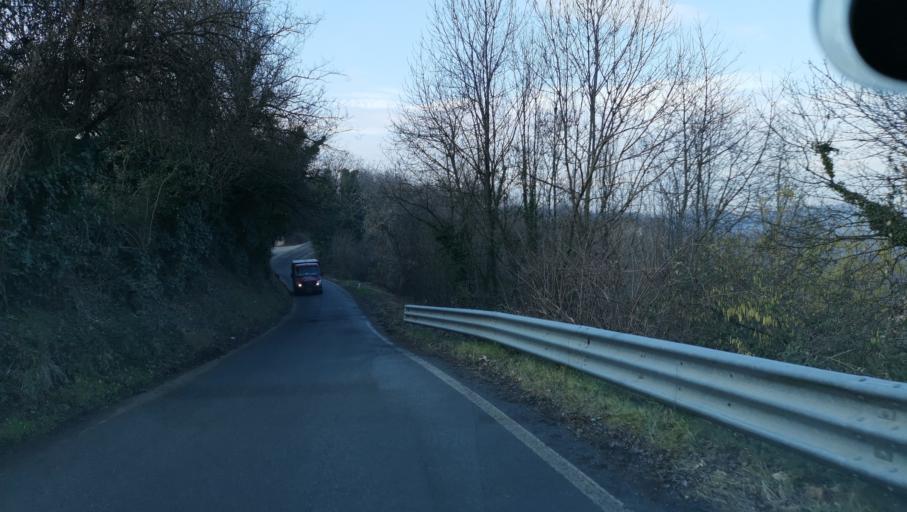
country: IT
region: Piedmont
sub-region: Provincia di Torino
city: Sciolze
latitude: 45.0974
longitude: 7.8631
